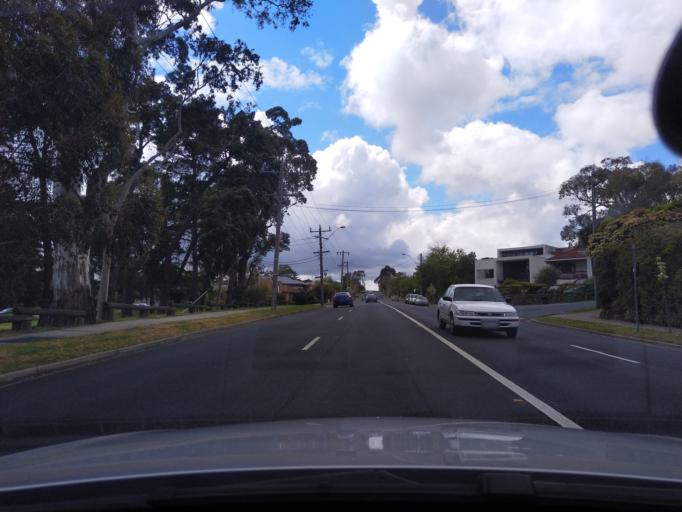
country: AU
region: Victoria
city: Macleod
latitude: -37.7414
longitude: 145.0676
